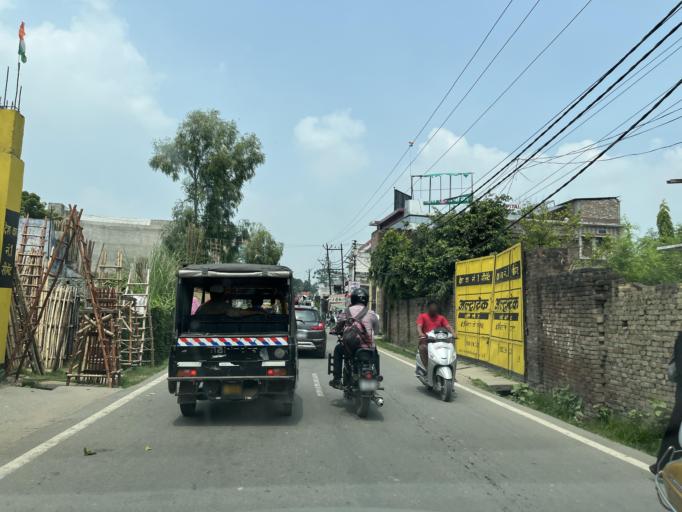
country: IN
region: Uttar Pradesh
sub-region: Bijnor
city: Najibabad
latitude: 29.6082
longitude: 78.3365
